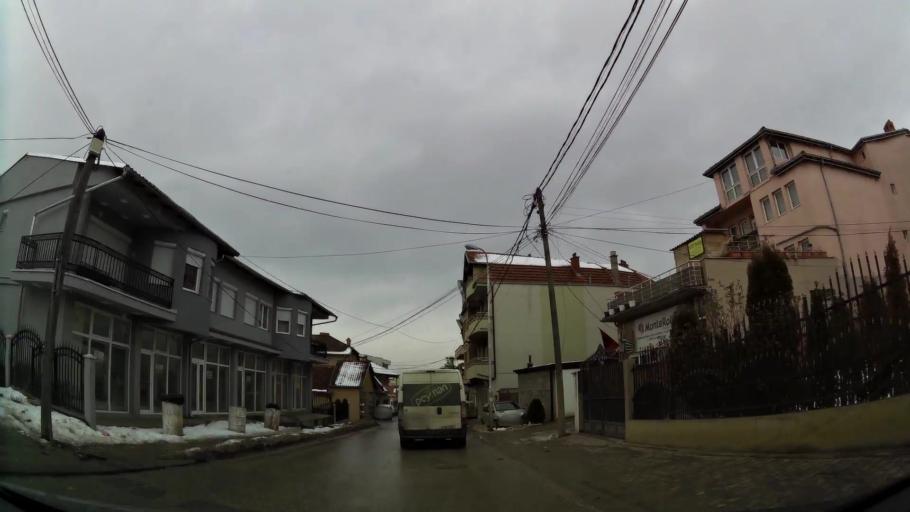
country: XK
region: Pristina
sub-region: Komuna e Prishtines
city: Pristina
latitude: 42.6587
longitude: 21.1832
